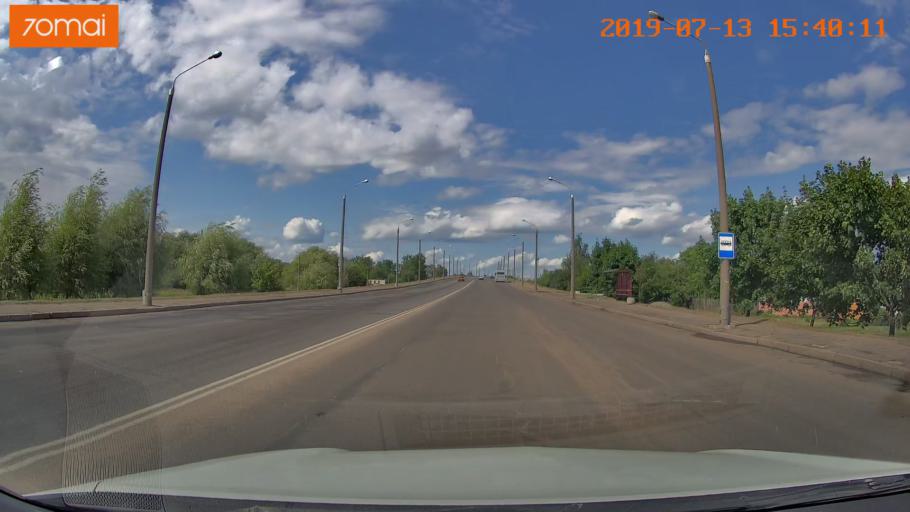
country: BY
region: Mogilev
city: Babruysk
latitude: 53.1355
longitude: 29.1890
